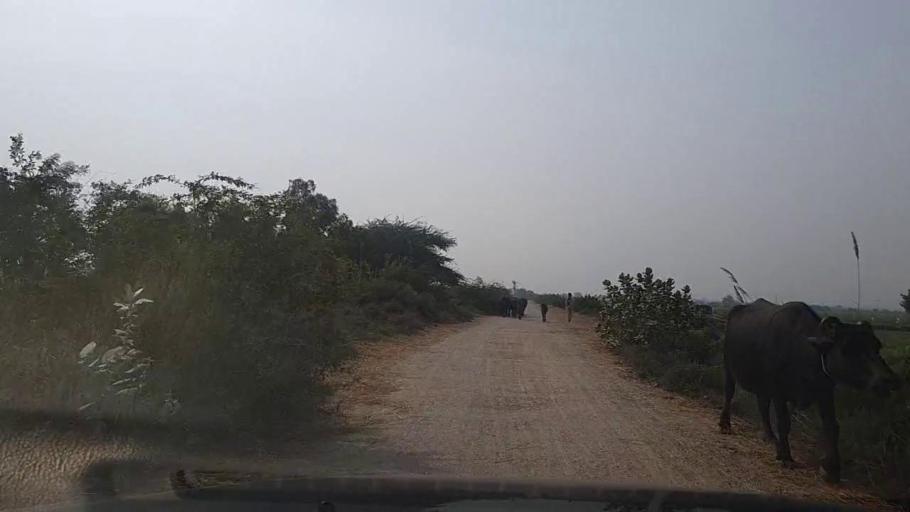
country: PK
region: Sindh
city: Mirpur Sakro
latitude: 24.5499
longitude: 67.8357
